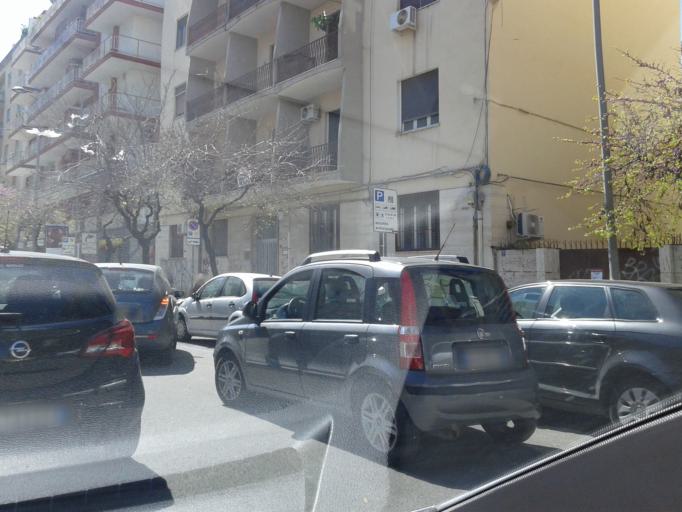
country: IT
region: Sicily
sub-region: Palermo
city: Palermo
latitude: 38.1344
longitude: 13.3419
